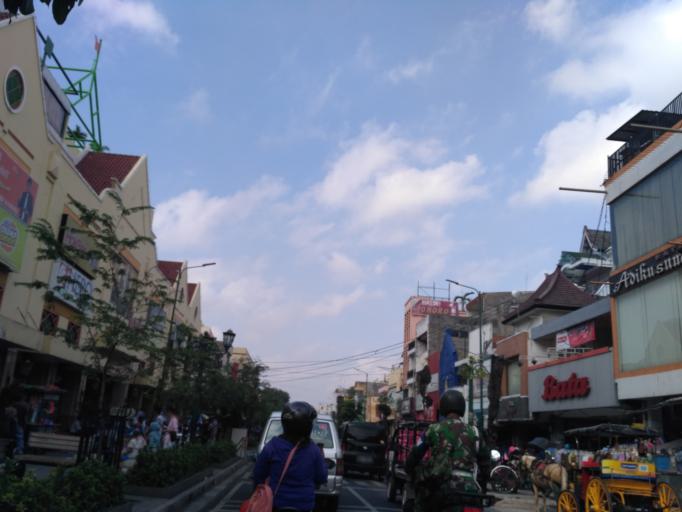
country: ID
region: Daerah Istimewa Yogyakarta
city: Yogyakarta
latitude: -7.7931
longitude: 110.3658
